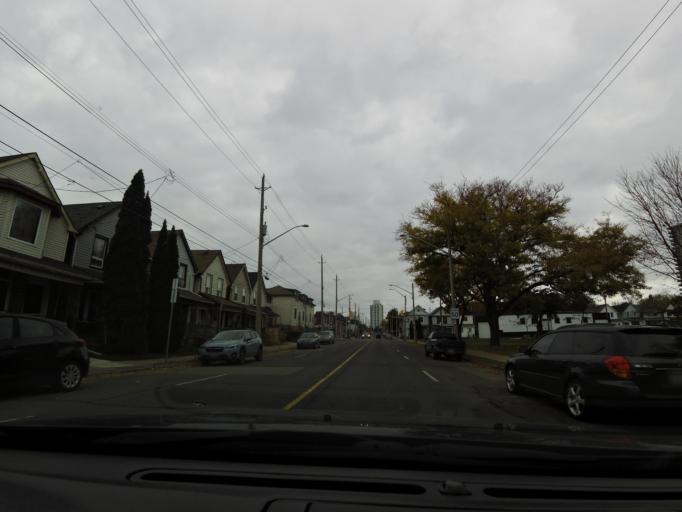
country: CA
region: Ontario
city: Hamilton
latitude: 43.2715
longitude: -79.8559
